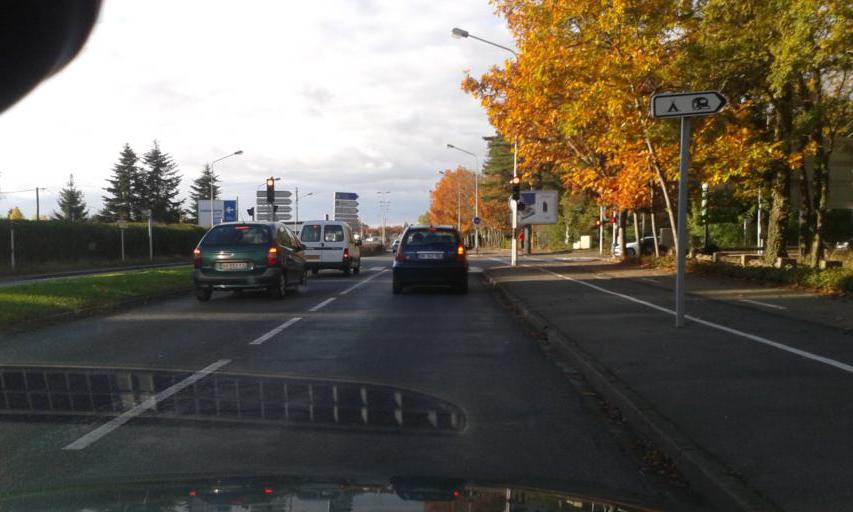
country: FR
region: Centre
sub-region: Departement du Loiret
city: Olivet
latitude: 47.8431
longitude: 1.9245
